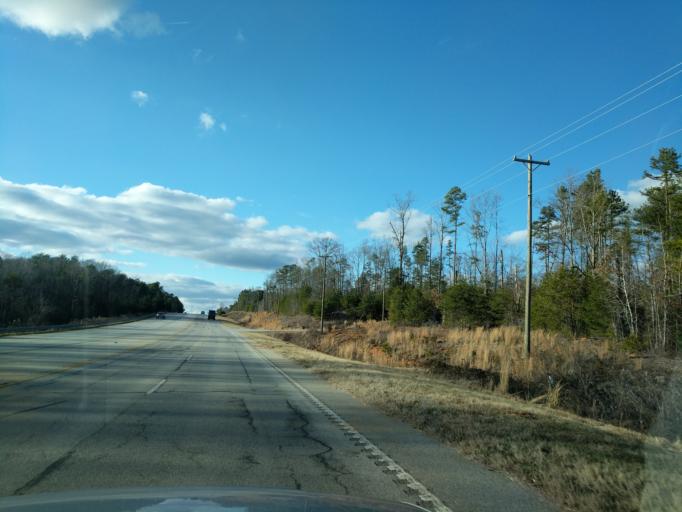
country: US
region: South Carolina
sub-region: Spartanburg County
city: Woodruff
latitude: 34.7752
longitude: -82.0812
